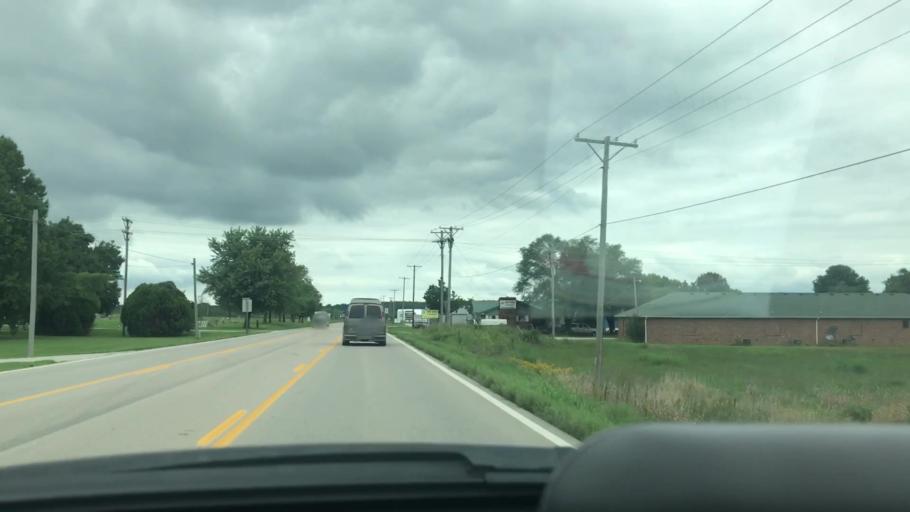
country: US
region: Missouri
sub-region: Dallas County
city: Buffalo
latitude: 37.6542
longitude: -93.1038
